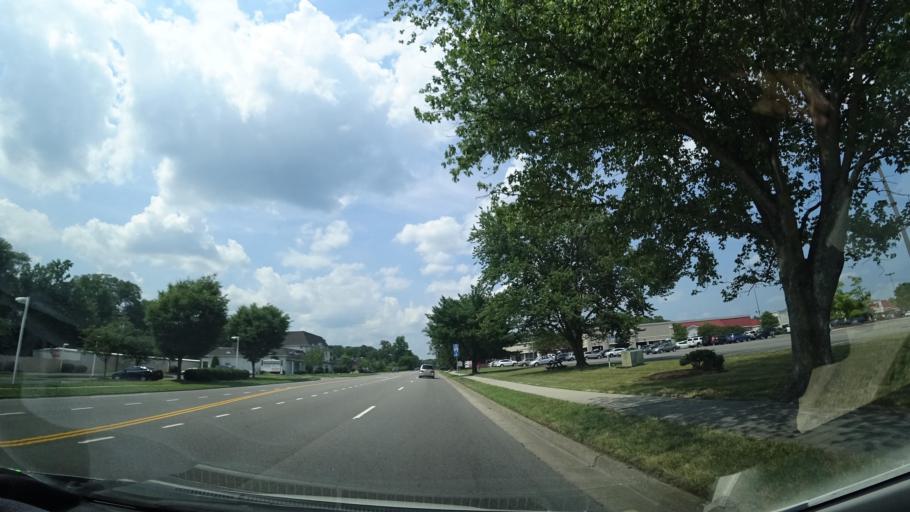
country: US
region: Virginia
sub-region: Hanover County
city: Ashland
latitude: 37.7599
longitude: -77.4715
